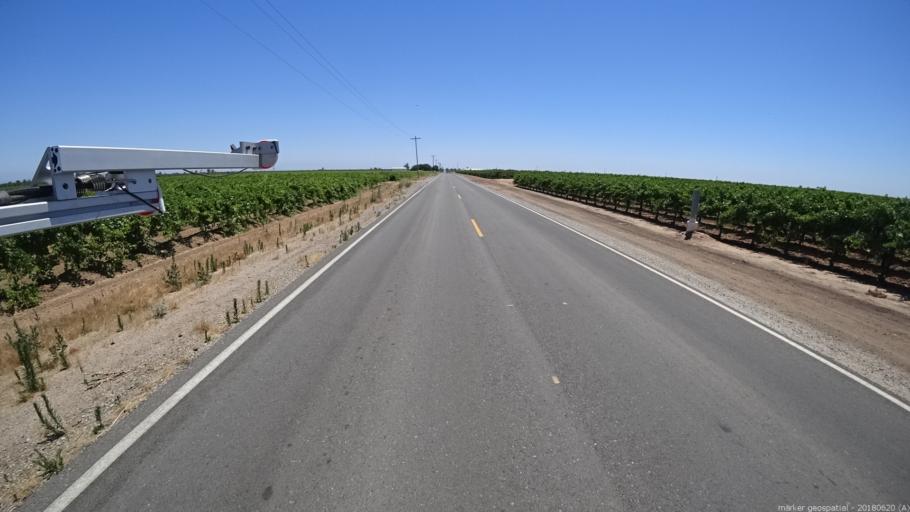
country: US
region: California
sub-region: Madera County
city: Parkwood
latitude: 36.8803
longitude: -119.9976
